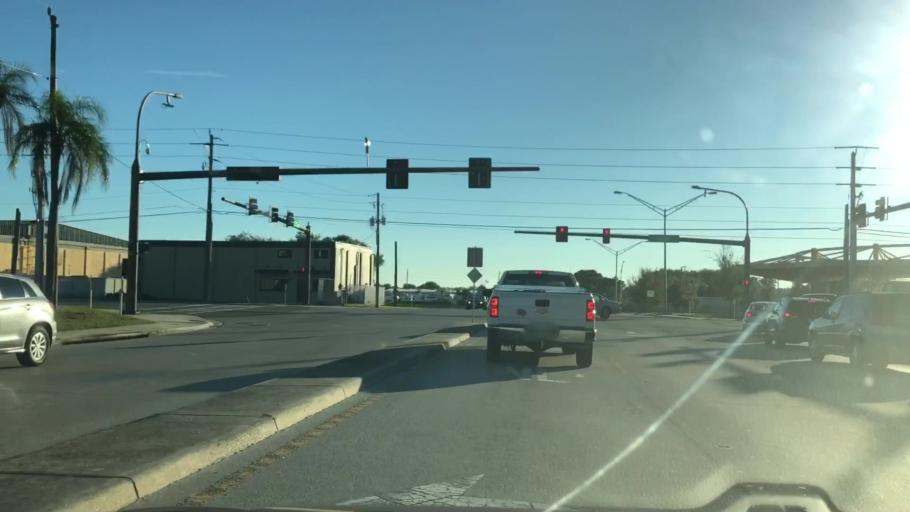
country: US
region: Florida
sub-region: Sarasota County
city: Fruitville
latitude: 27.3230
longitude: -82.4519
